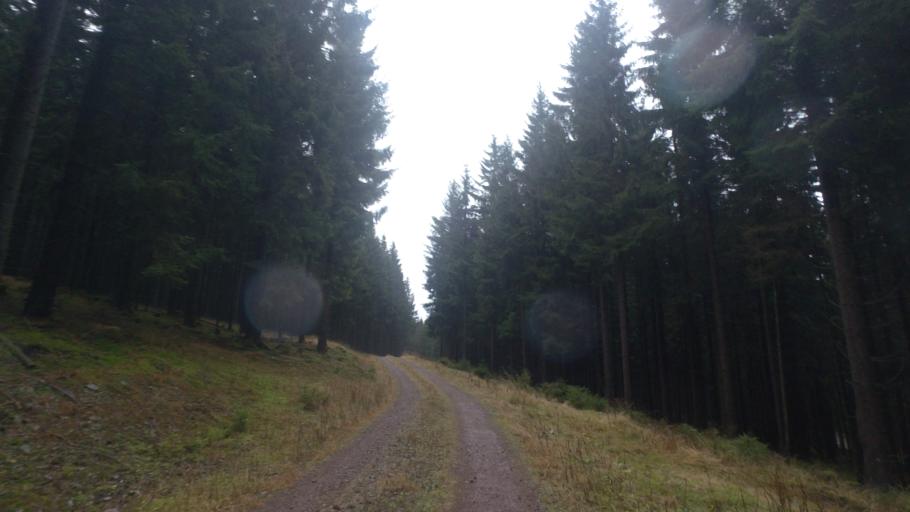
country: DE
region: Thuringia
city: Oberhof
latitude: 50.7207
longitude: 10.7598
